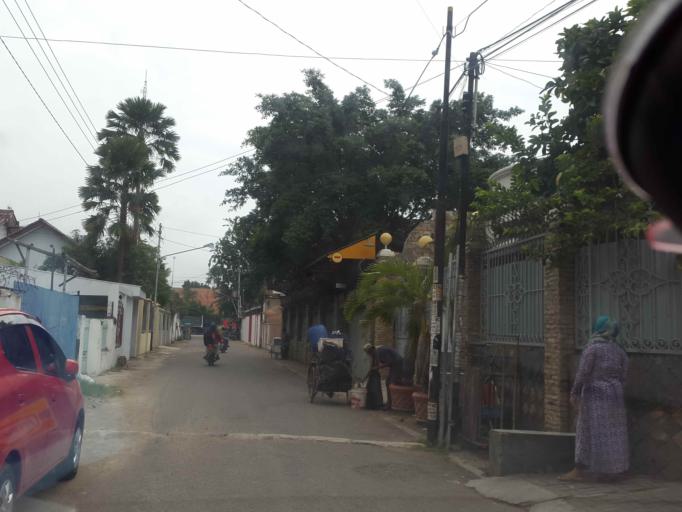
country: ID
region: Central Java
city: Tegal
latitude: -6.8650
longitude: 109.1349
